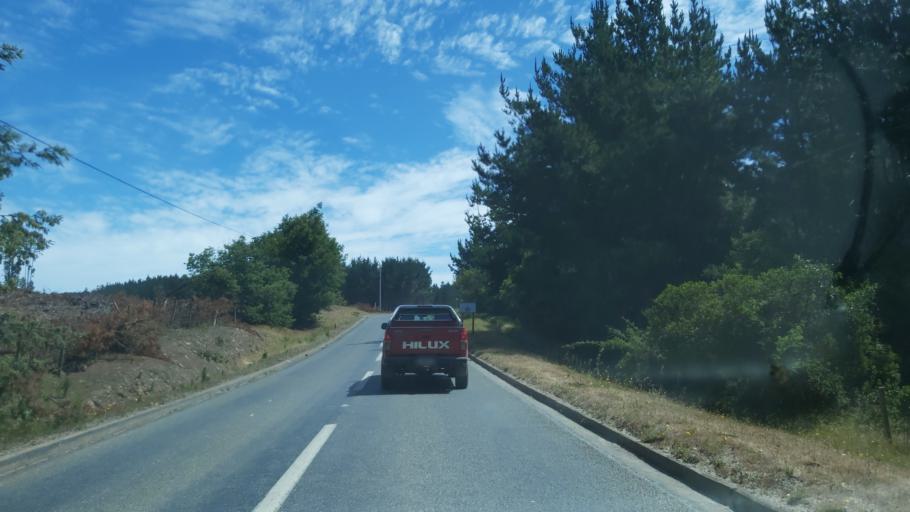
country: CL
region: Maule
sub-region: Provincia de Talca
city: Constitucion
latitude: -35.5490
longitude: -72.5661
